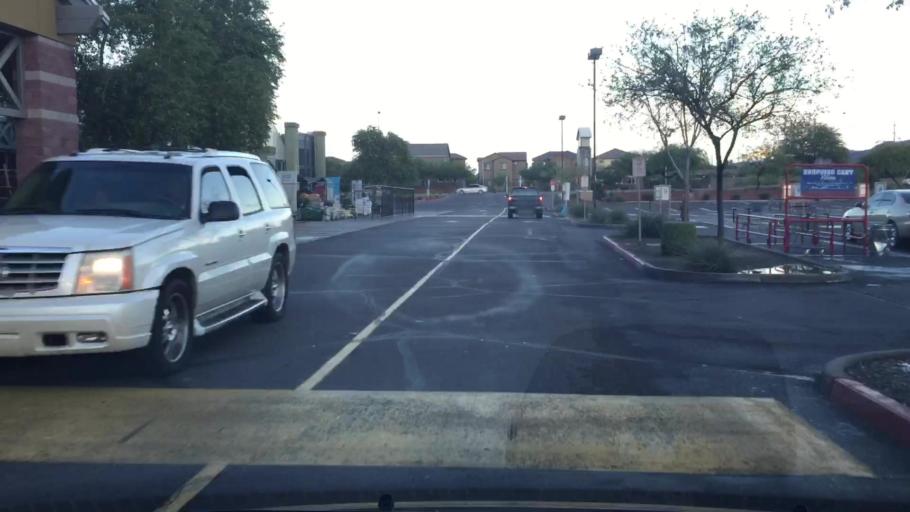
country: US
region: Arizona
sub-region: Maricopa County
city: Laveen
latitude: 33.3799
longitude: -112.1005
